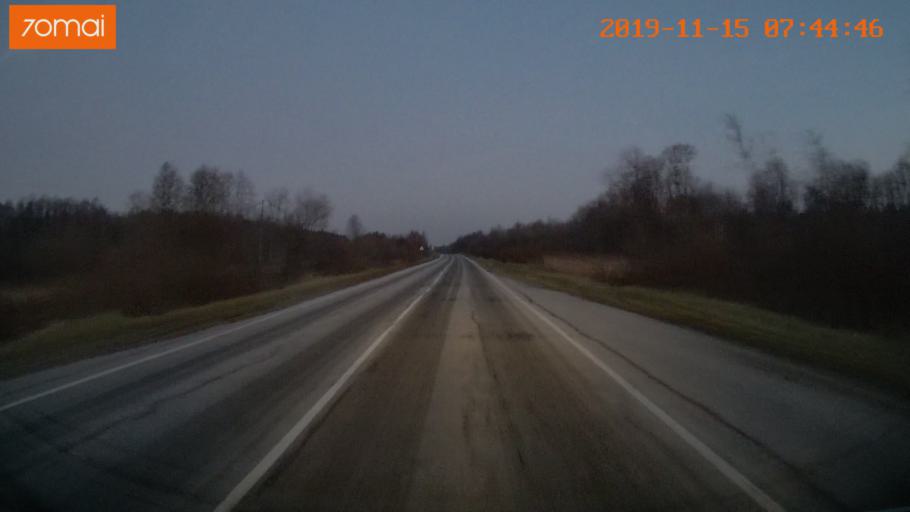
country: RU
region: Vologda
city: Sheksna
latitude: 58.8163
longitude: 38.3091
